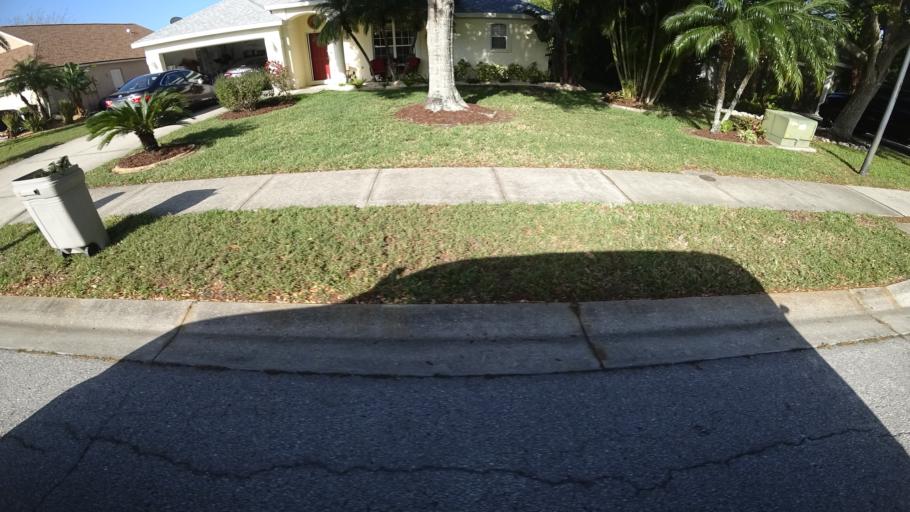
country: US
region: Florida
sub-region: Manatee County
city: Whitfield
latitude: 27.4120
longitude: -82.5575
